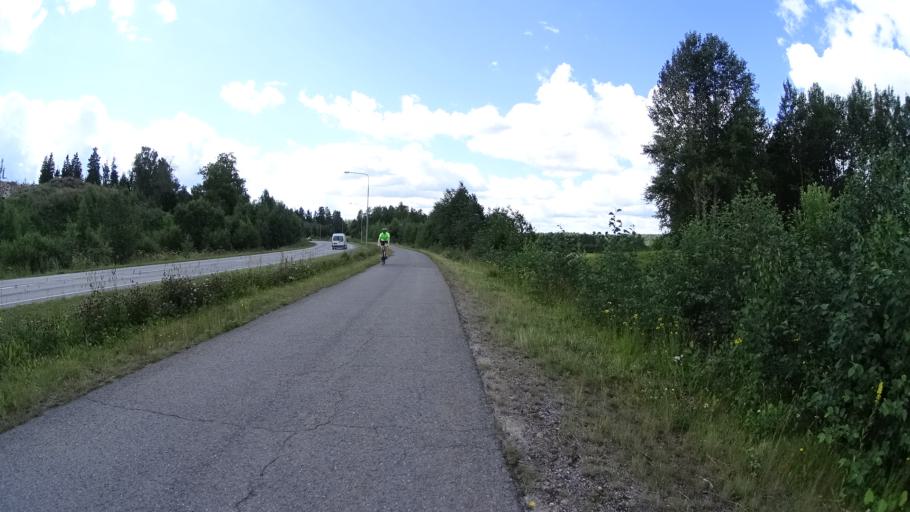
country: FI
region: Uusimaa
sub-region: Helsinki
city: Teekkarikylae
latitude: 60.3070
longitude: 24.8849
